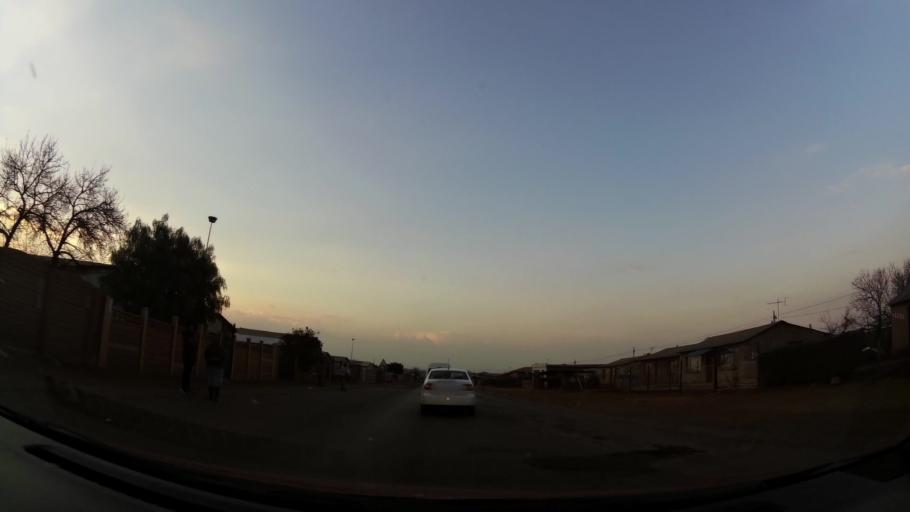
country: ZA
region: Gauteng
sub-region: City of Johannesburg Metropolitan Municipality
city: Orange Farm
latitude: -26.5569
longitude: 27.8622
